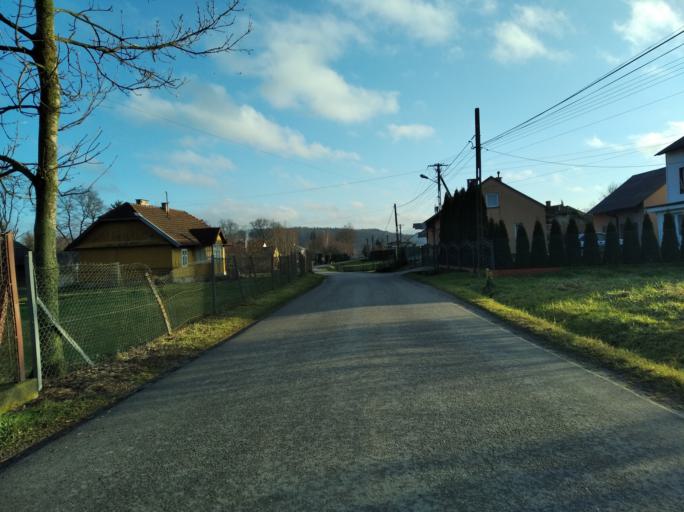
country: PL
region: Subcarpathian Voivodeship
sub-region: Powiat strzyzowski
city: Czudec
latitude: 49.9428
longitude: 21.8103
